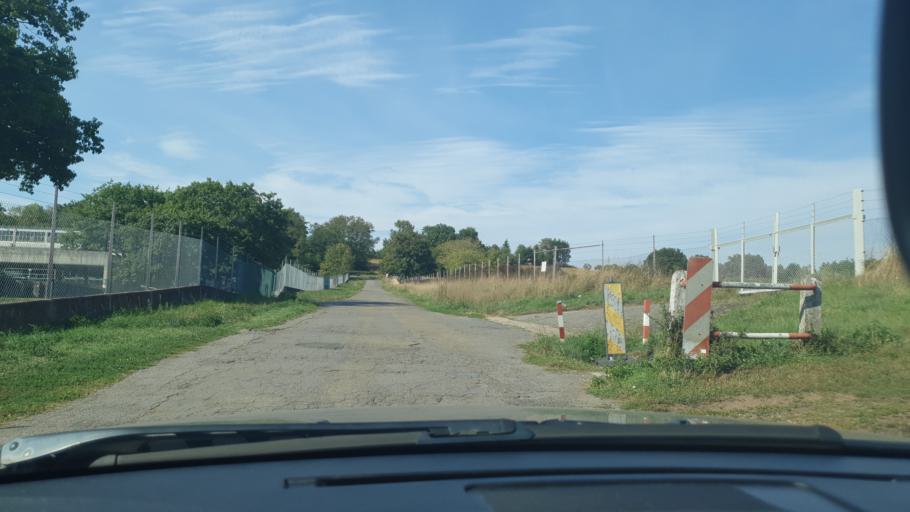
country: DE
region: Rheinland-Pfalz
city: Zweibrucken
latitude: 49.2609
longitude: 7.3884
